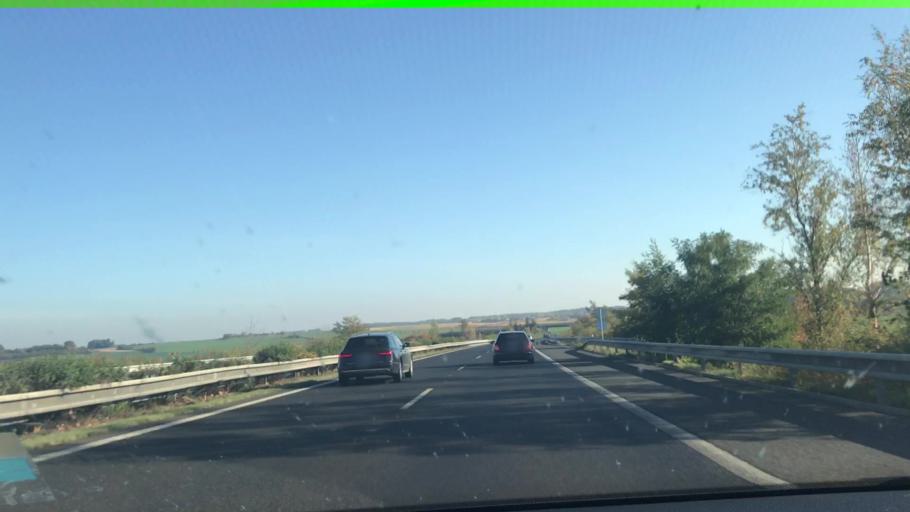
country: CZ
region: Ustecky
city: Roudnice nad Labem
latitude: 50.3608
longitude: 14.2671
